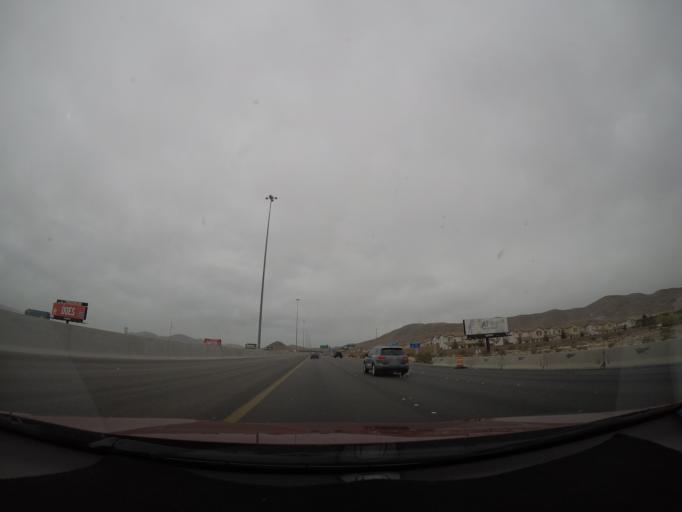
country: US
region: Nevada
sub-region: Clark County
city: Enterprise
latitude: 35.9727
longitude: -115.1816
